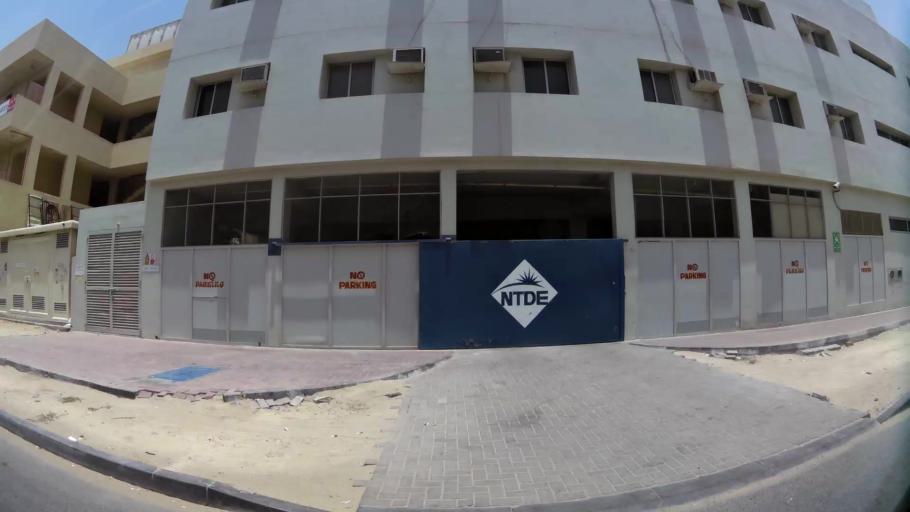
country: AE
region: Ash Shariqah
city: Sharjah
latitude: 25.2664
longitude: 55.4311
